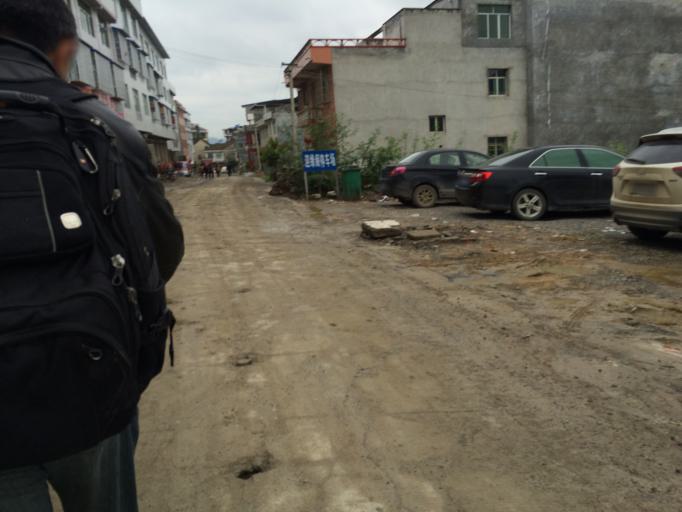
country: CN
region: Guizhou Sheng
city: Dalucao
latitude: 27.8329
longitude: 107.2532
